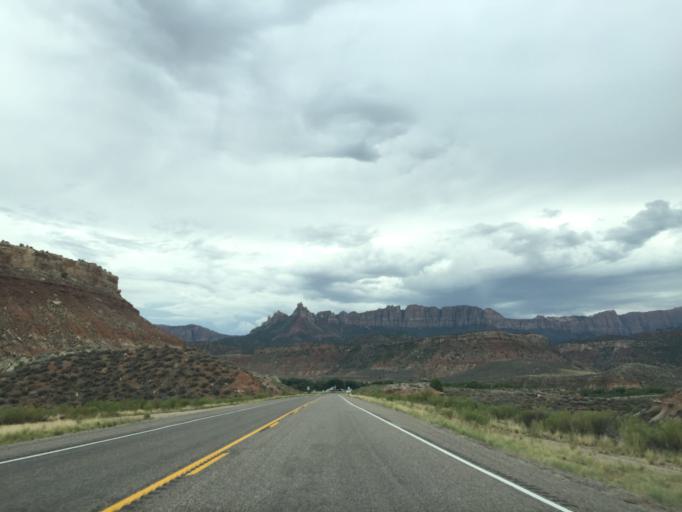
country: US
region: Utah
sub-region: Washington County
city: Hildale
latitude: 37.1673
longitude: -113.0641
